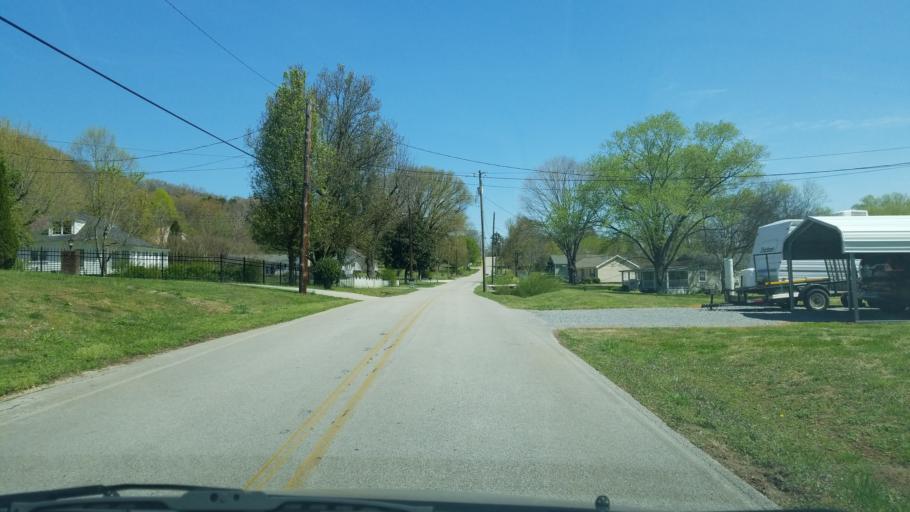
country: US
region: Tennessee
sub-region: Hamilton County
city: Soddy-Daisy
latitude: 35.2325
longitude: -85.2105
